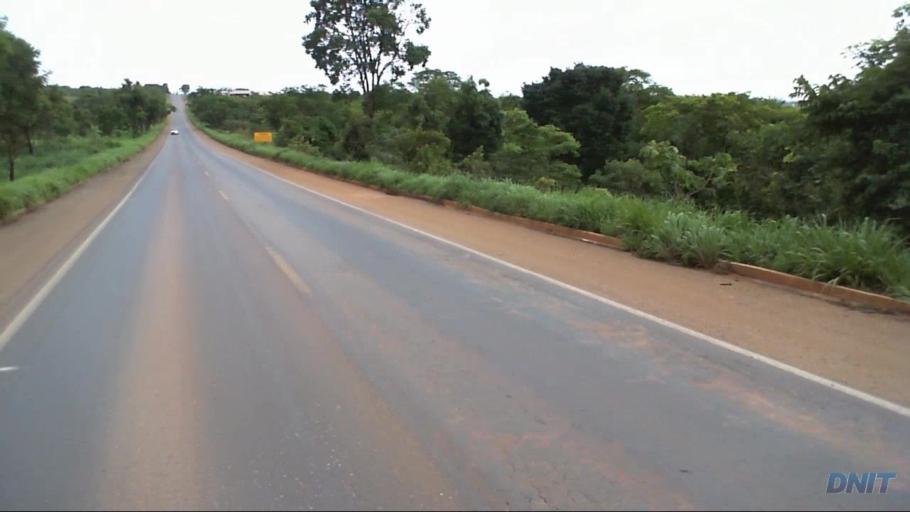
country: BR
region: Goias
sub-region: Uruacu
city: Uruacu
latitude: -14.5539
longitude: -49.1589
